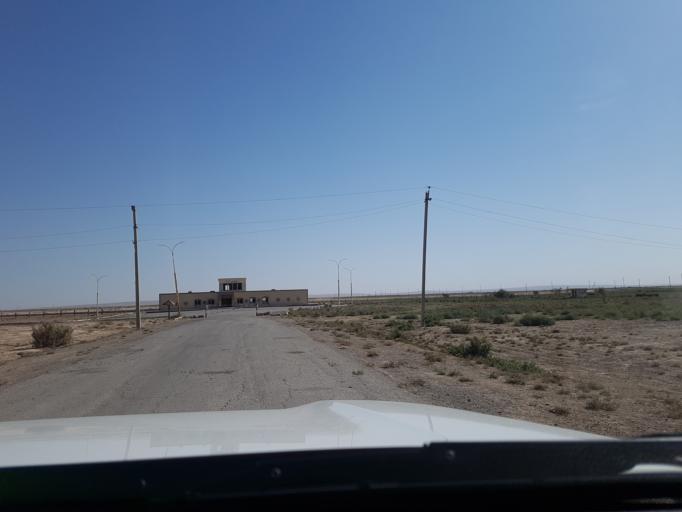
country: IR
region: Razavi Khorasan
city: Sarakhs
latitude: 36.4928
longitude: 61.2546
